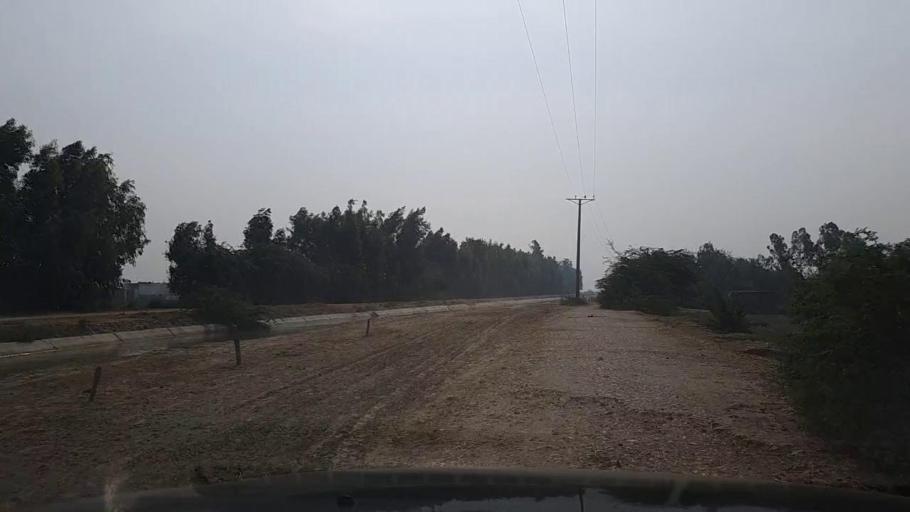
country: PK
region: Sindh
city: Mirpur Sakro
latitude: 24.5372
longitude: 67.8121
